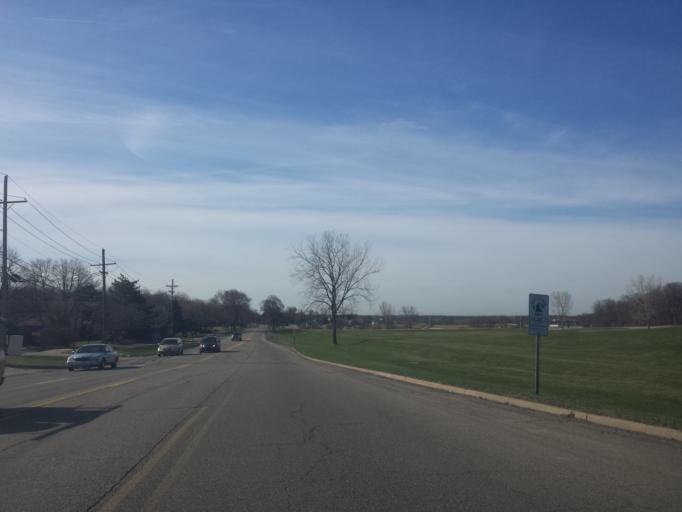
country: US
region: Michigan
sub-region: Oakland County
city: Auburn Hills
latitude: 42.6802
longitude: -83.1941
